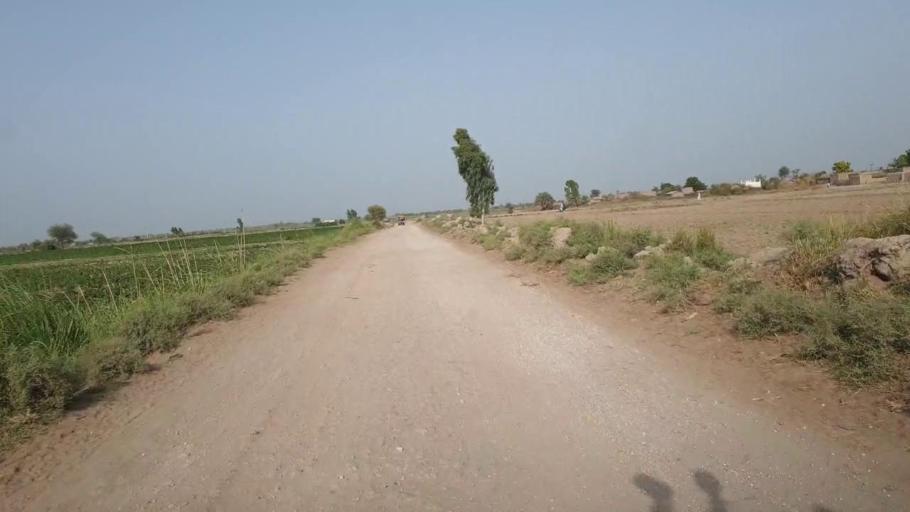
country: PK
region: Sindh
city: Daur
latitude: 26.3405
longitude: 68.2056
